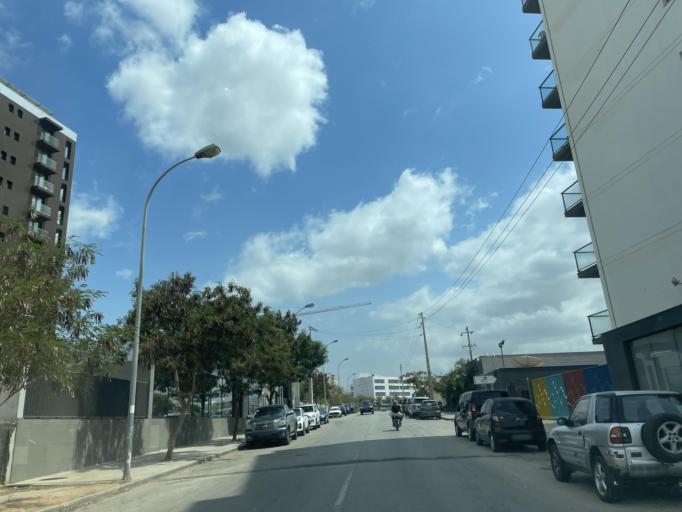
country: AO
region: Luanda
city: Luanda
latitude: -8.9265
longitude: 13.1930
